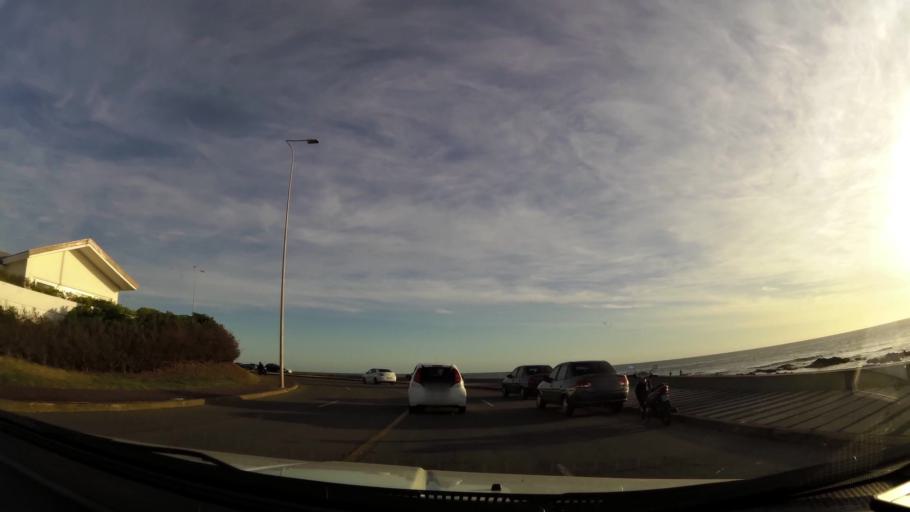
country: UY
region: Maldonado
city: Punta del Este
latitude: -34.9717
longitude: -54.9538
